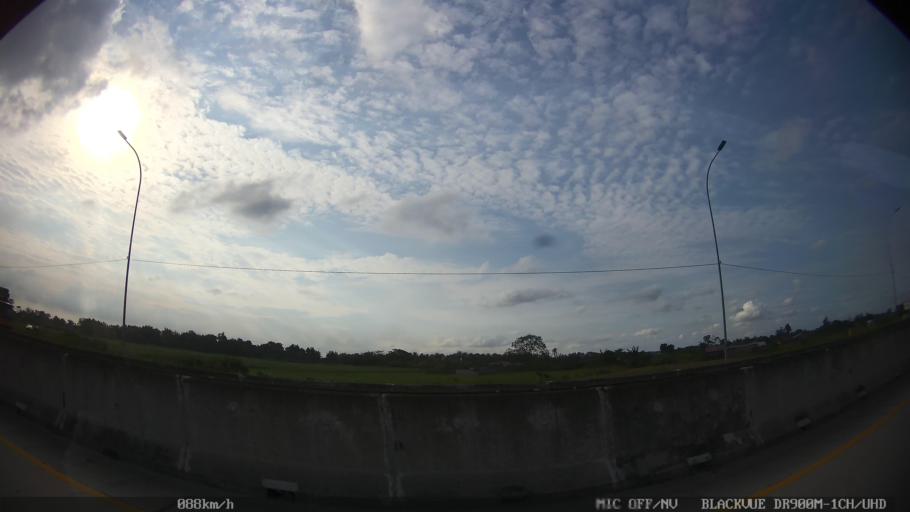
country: ID
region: North Sumatra
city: Medan
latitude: 3.6416
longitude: 98.6465
